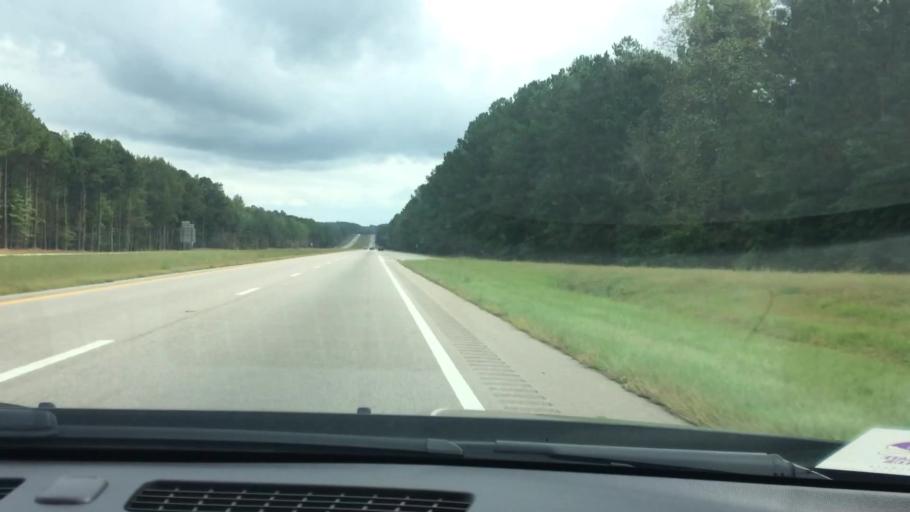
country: US
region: North Carolina
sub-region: Wake County
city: Zebulon
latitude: 35.8198
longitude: -78.2661
